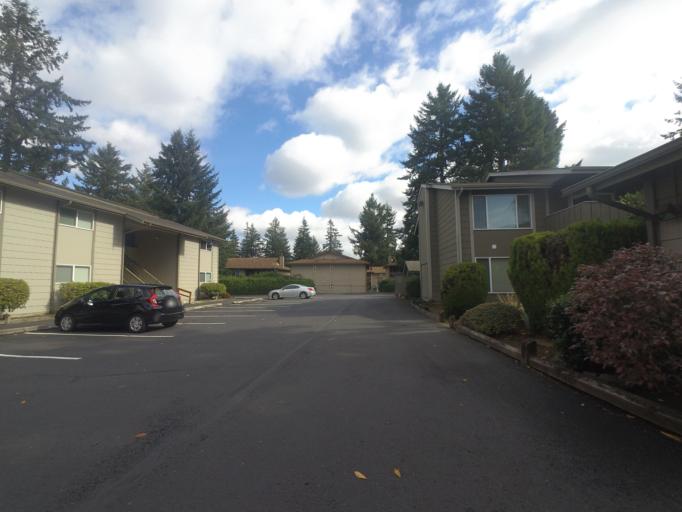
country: US
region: Washington
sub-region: Pierce County
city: University Place
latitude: 47.2181
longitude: -122.5403
